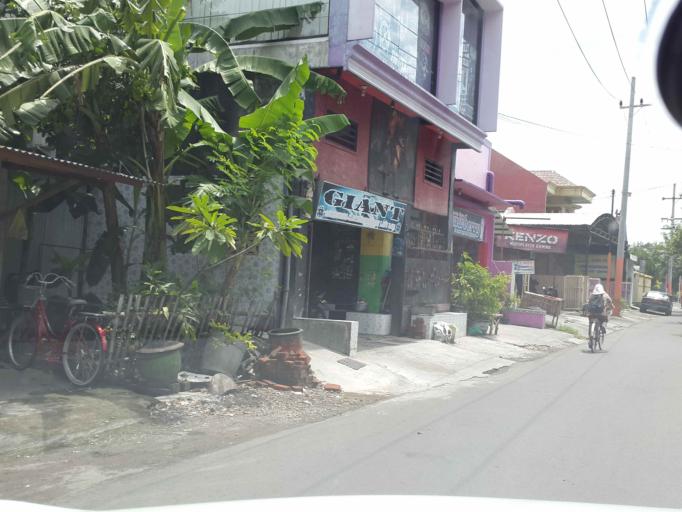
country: ID
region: East Java
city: Mojokerto
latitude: -7.4595
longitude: 112.4442
